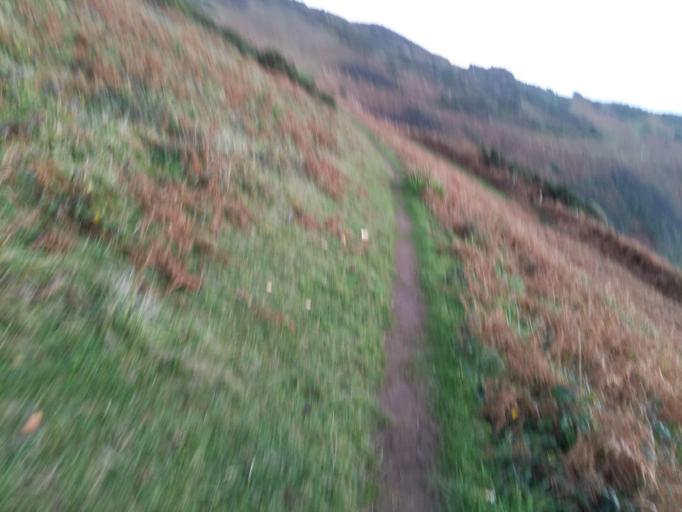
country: GB
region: England
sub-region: Cornwall
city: Fowey
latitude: 50.3280
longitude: -4.6021
